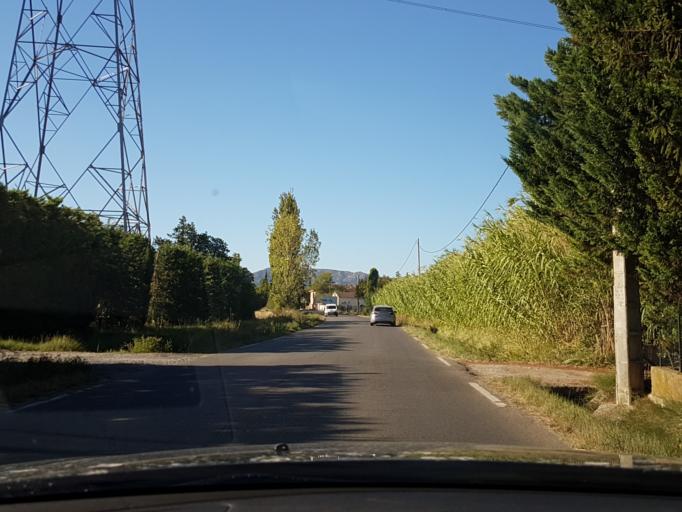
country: FR
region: Provence-Alpes-Cote d'Azur
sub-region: Departement des Bouches-du-Rhone
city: Molleges
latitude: 43.7914
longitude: 4.9540
